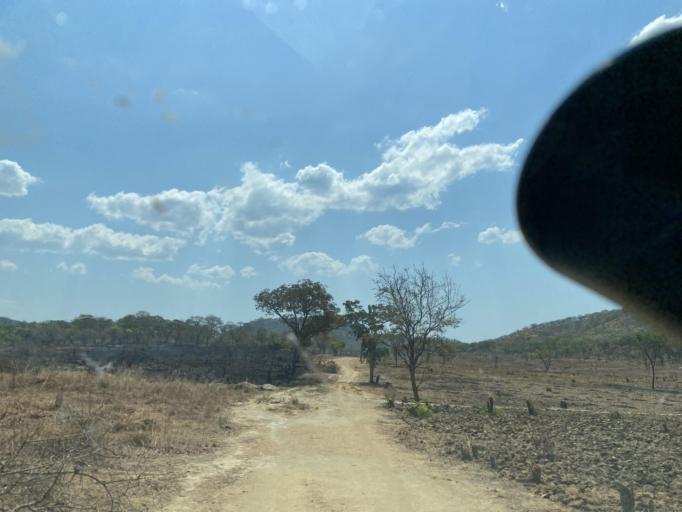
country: ZM
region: Lusaka
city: Chongwe
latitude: -15.0844
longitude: 29.4803
